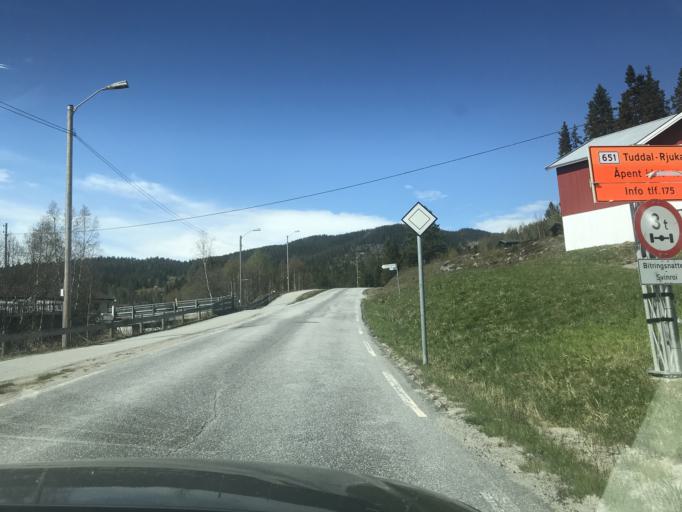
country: NO
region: Telemark
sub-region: Hjartdal
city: Sauland
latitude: 59.7556
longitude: 8.7890
